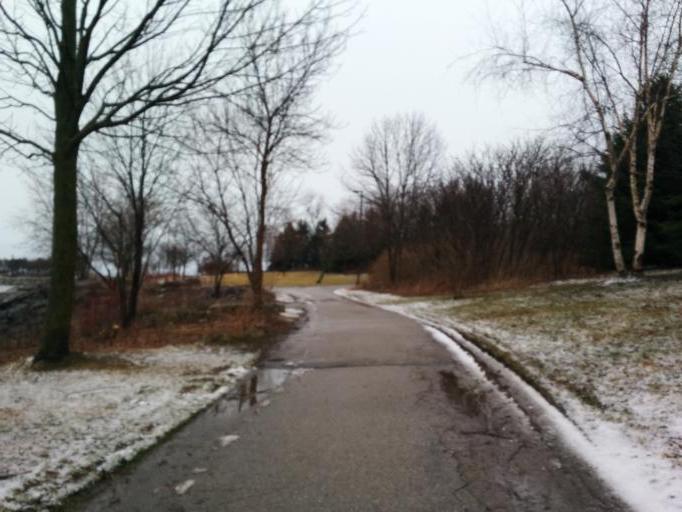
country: CA
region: Ontario
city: Etobicoke
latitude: 43.5636
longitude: -79.5625
